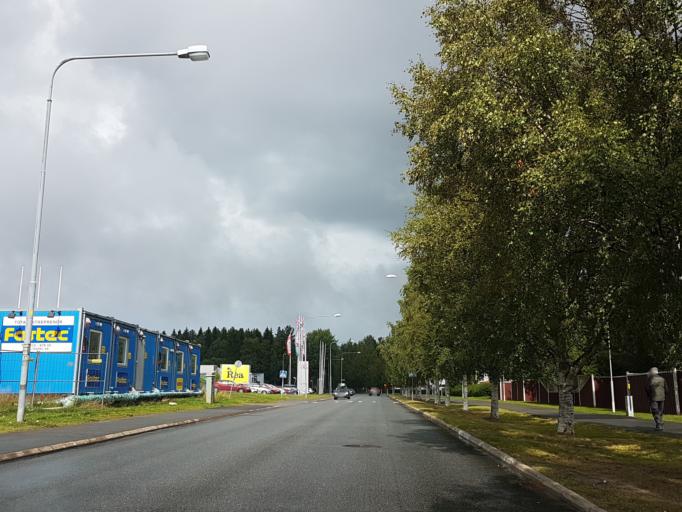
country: SE
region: Vaesterbotten
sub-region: Umea Kommun
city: Ersmark
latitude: 63.8542
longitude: 20.3027
